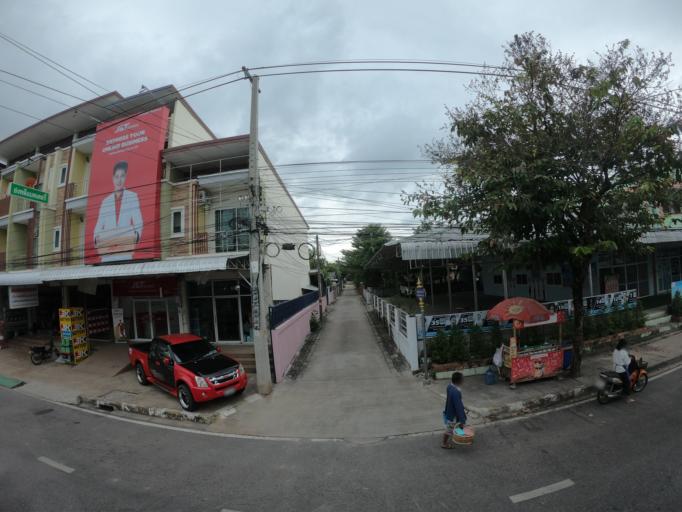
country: TH
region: Roi Et
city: Roi Et
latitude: 16.0499
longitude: 103.6400
